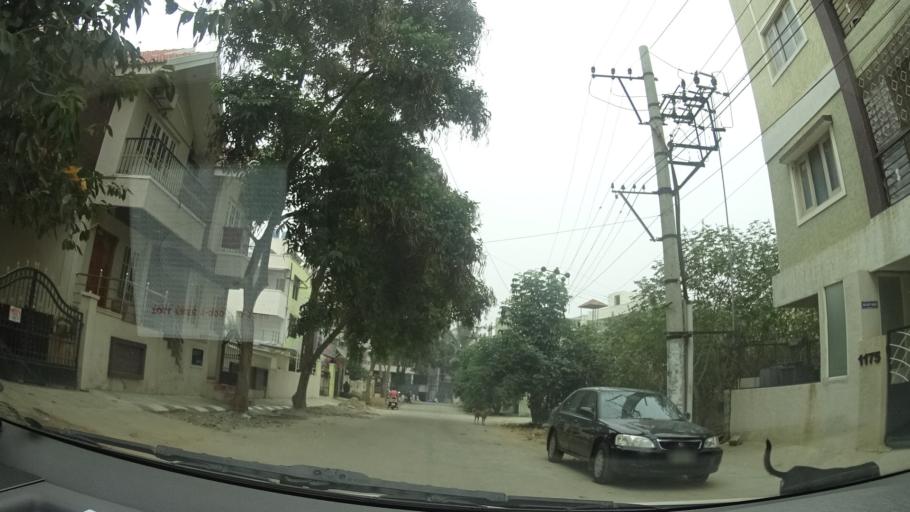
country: IN
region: Karnataka
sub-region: Bangalore Urban
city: Bangalore
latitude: 13.0306
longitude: 77.6324
